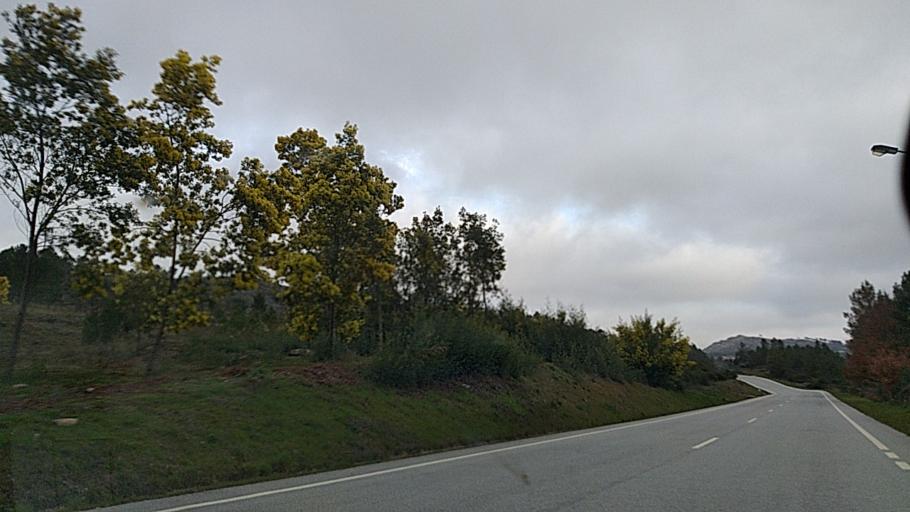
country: PT
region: Guarda
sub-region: Fornos de Algodres
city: Fornos de Algodres
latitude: 40.6426
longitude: -7.4928
